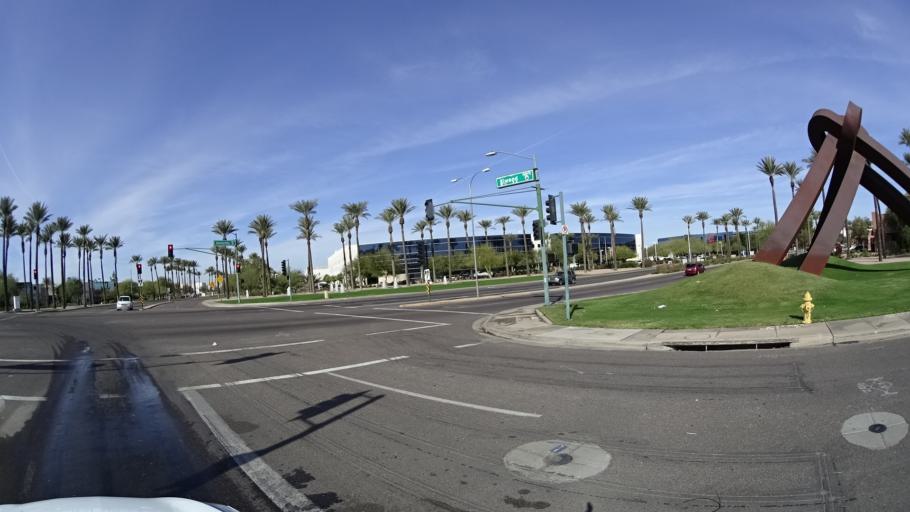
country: US
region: Arizona
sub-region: Maricopa County
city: Guadalupe
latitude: 33.4147
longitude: -112.0087
